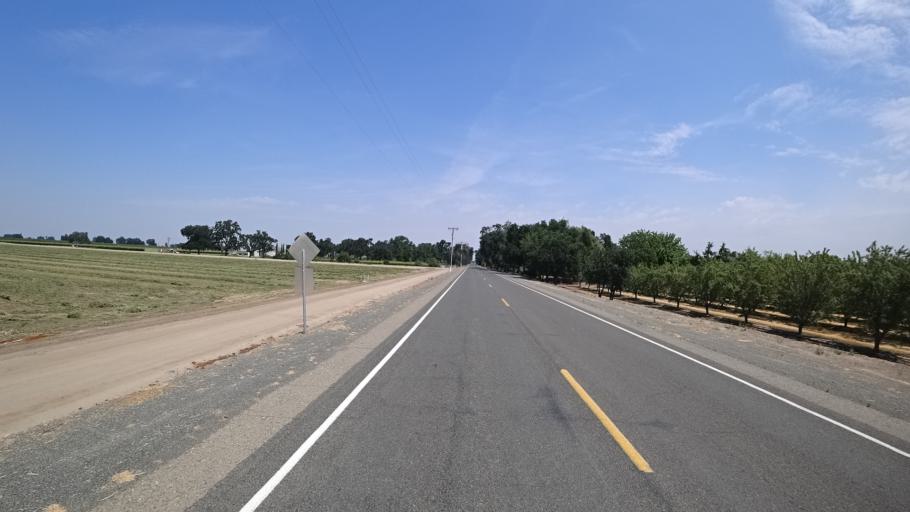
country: US
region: California
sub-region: Kings County
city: Lemoore
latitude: 36.3631
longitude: -119.7810
